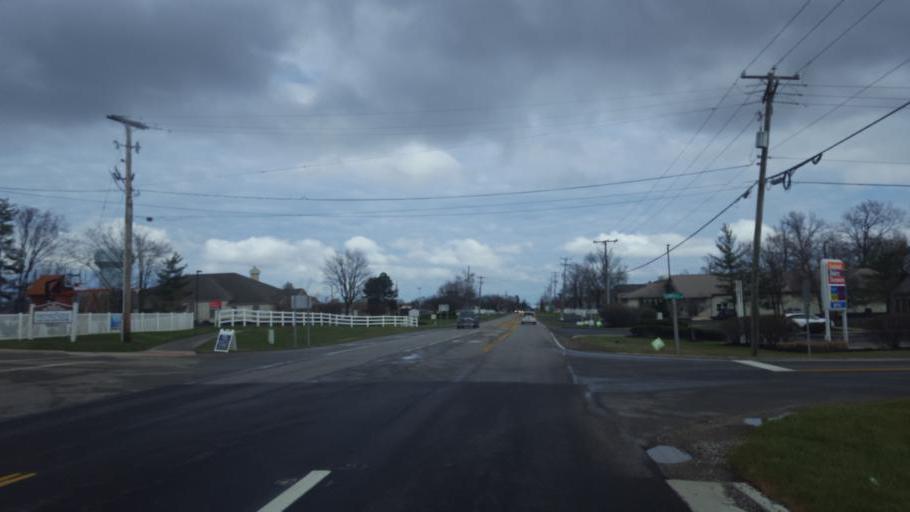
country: US
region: Ohio
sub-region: Delaware County
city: Powell
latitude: 40.1584
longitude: -83.0887
